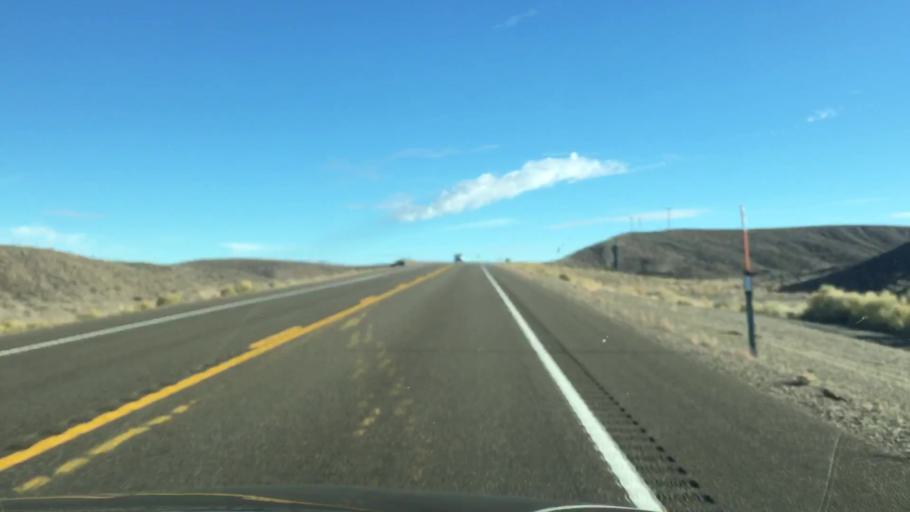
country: US
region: Nevada
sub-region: Mineral County
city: Hawthorne
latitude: 38.2206
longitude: -118.0086
